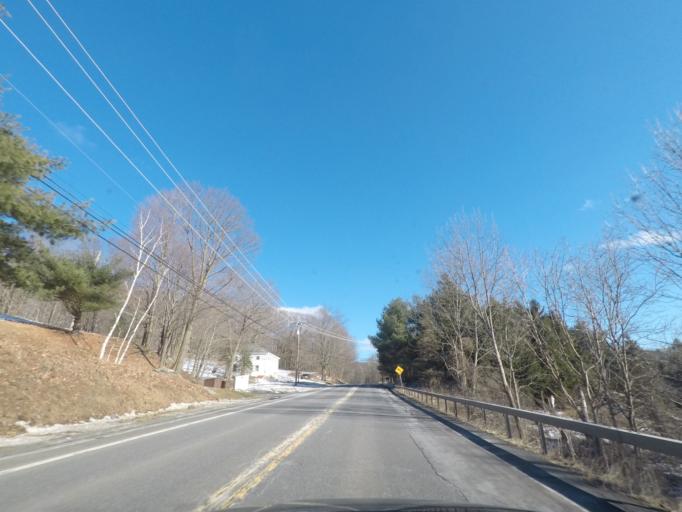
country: US
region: New York
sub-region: Columbia County
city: Chatham
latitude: 42.3192
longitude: -73.5065
